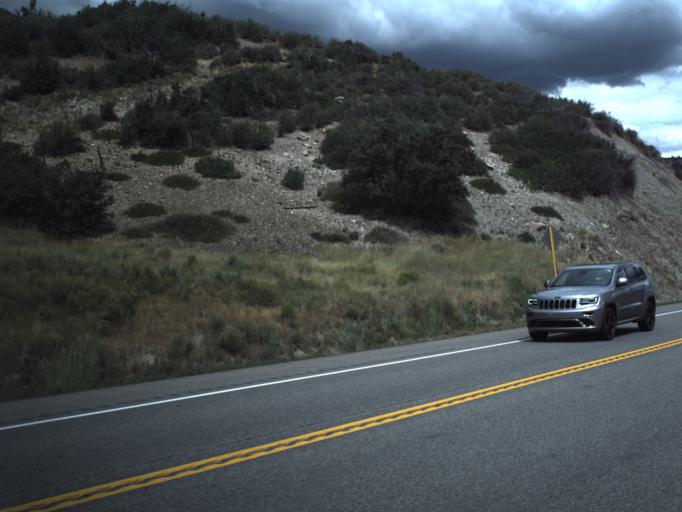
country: US
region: Utah
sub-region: Carbon County
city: Helper
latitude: 39.9339
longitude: -111.1239
